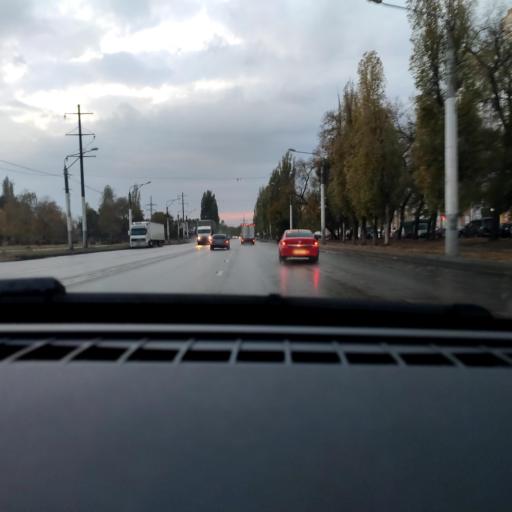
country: RU
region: Voronezj
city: Maslovka
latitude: 51.6008
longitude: 39.2419
